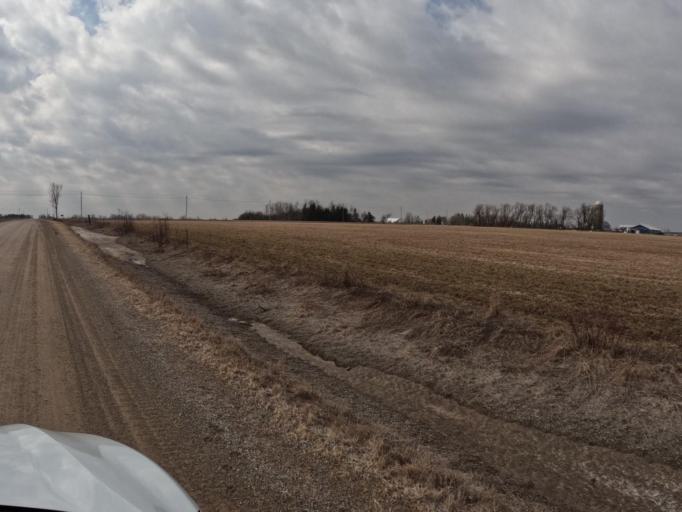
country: CA
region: Ontario
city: Orangeville
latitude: 43.9232
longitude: -80.2186
